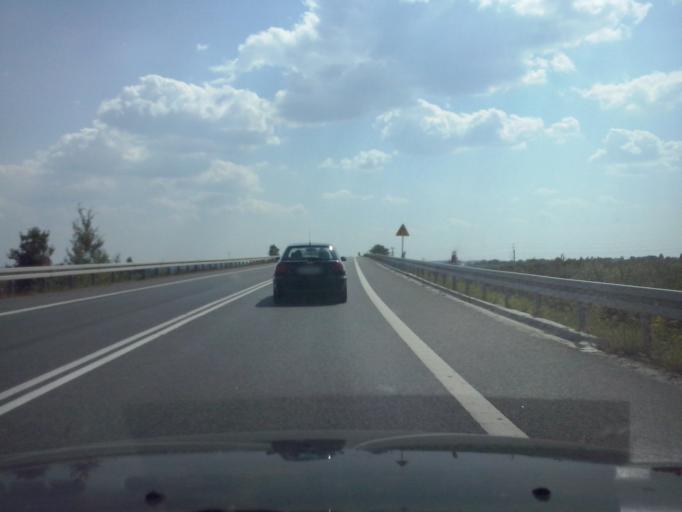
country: PL
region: Subcarpathian Voivodeship
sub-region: Powiat tarnobrzeski
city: Baranow Sandomierski
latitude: 50.5358
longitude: 21.5719
